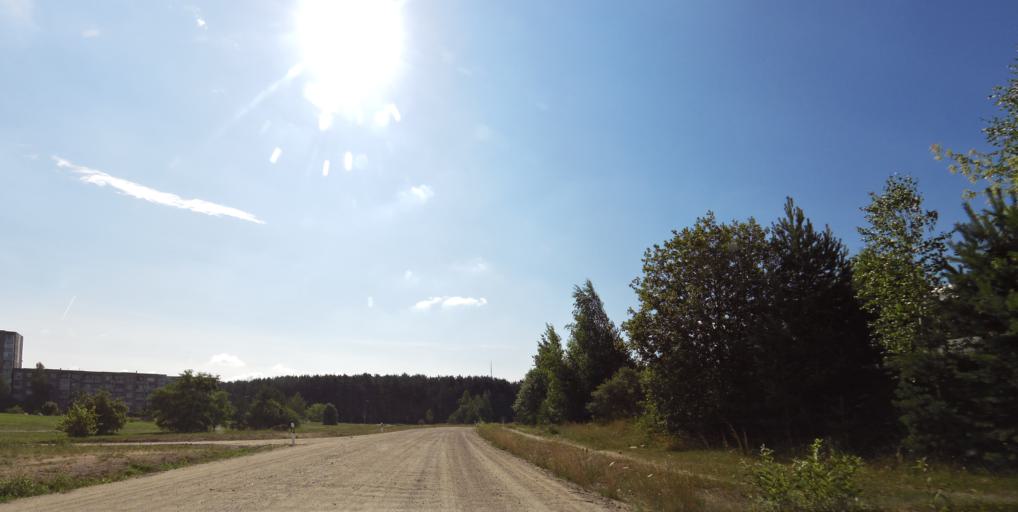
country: LT
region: Vilnius County
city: Pilaite
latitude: 54.7019
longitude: 25.1788
